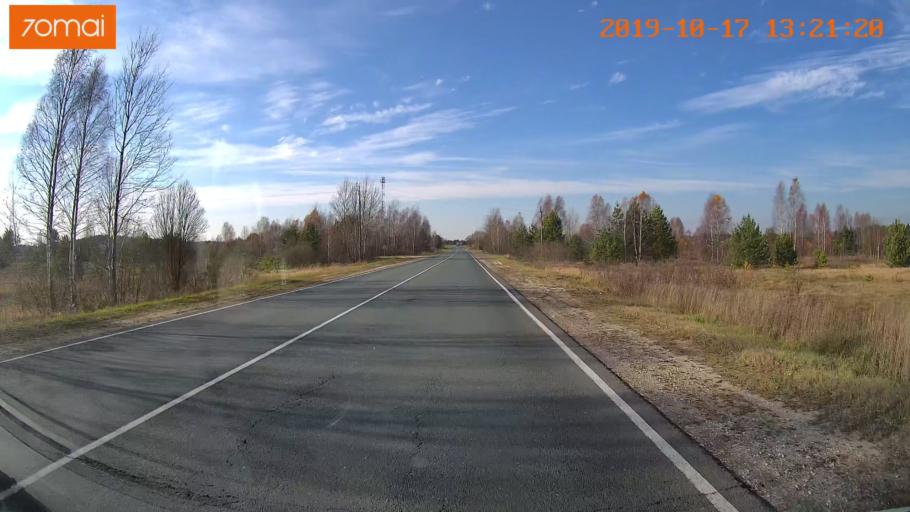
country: RU
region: Rjazan
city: Gus'-Zheleznyy
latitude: 55.0806
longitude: 41.0296
